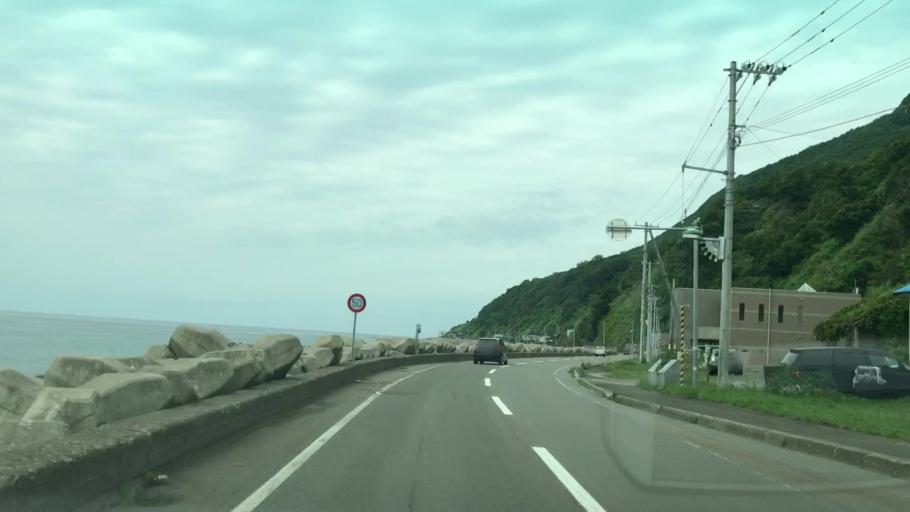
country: JP
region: Hokkaido
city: Iwanai
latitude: 43.1578
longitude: 140.4027
